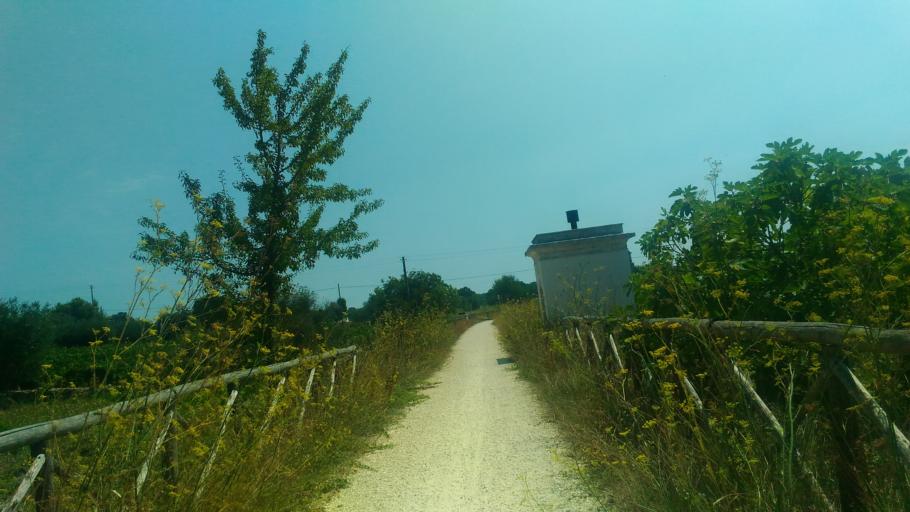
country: IT
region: Apulia
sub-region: Provincia di Brindisi
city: Cisternino
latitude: 40.7379
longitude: 17.3854
